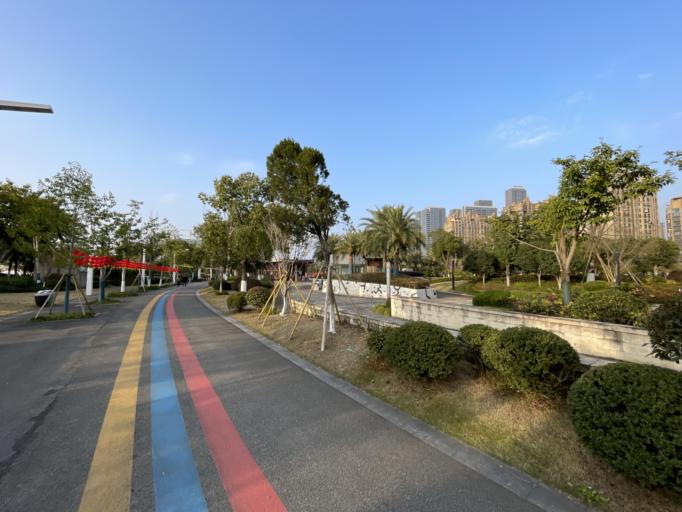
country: CN
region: Zhejiang Sheng
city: Wenzhou
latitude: 27.9746
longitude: 120.6949
